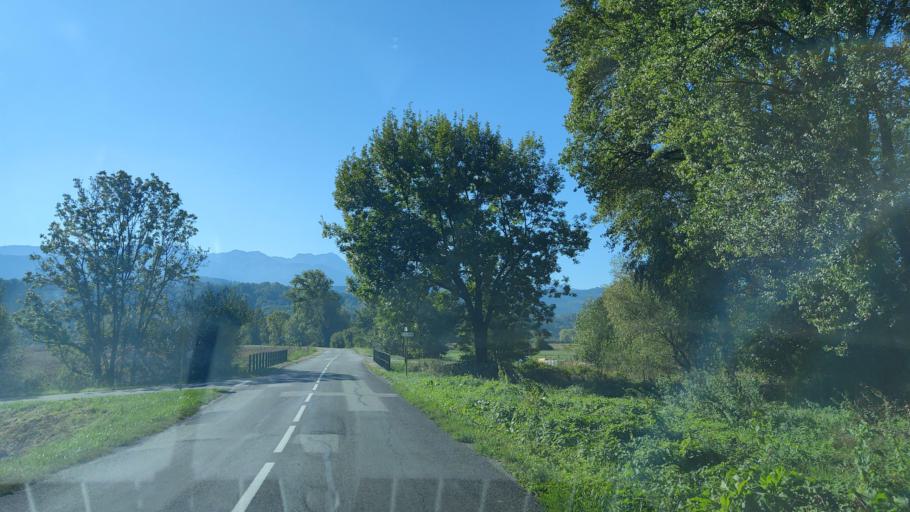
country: FR
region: Rhone-Alpes
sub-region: Departement de la Savoie
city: Coise-Saint-Jean-Pied-Gauthier
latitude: 45.5486
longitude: 6.1290
